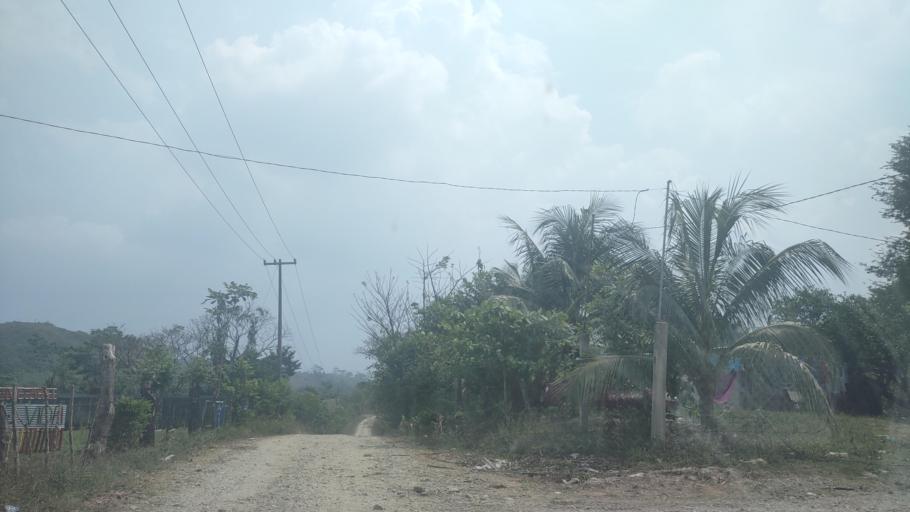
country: MX
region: Tabasco
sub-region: Huimanguillo
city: Francisco Rueda
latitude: 17.6664
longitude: -93.8856
